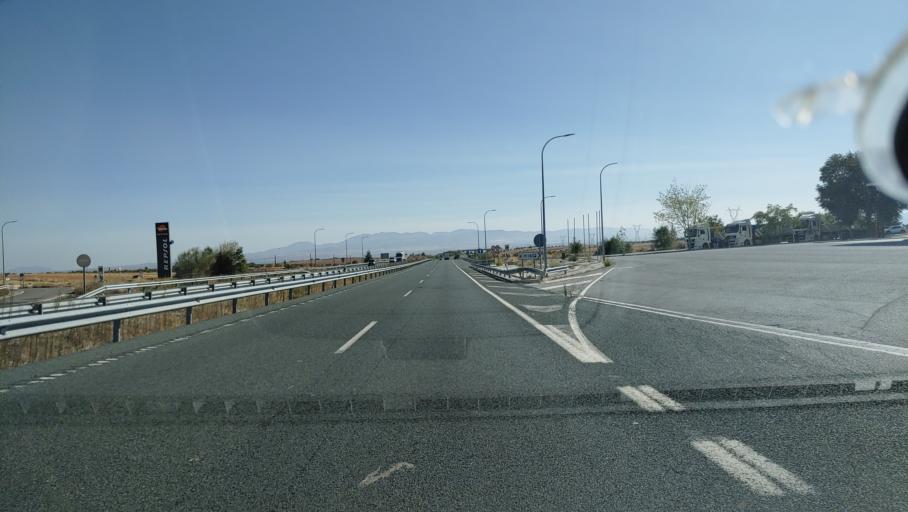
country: ES
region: Andalusia
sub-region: Provincia de Granada
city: Darro
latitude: 37.3208
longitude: -3.2981
